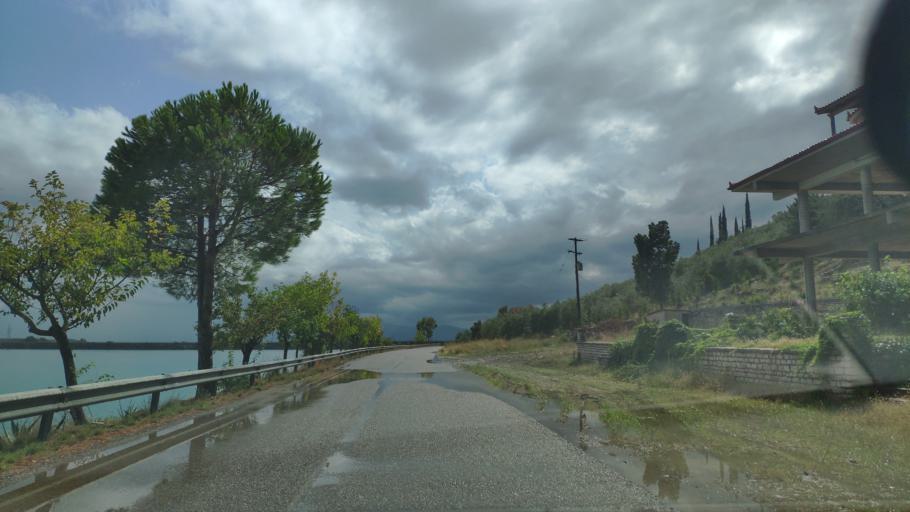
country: GR
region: West Greece
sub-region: Nomos Aitolias kai Akarnanias
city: Neapolis
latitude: 38.6820
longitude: 21.3235
